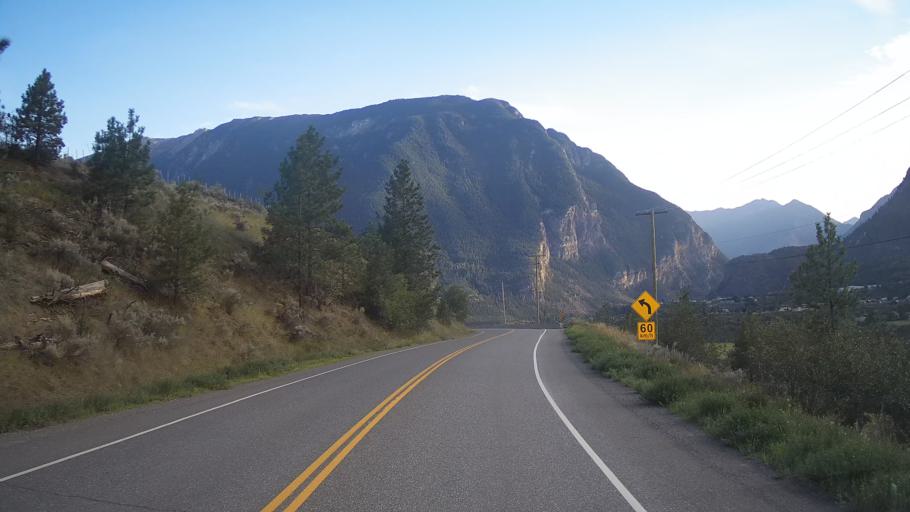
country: CA
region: British Columbia
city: Lillooet
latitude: 50.6949
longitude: -121.9195
